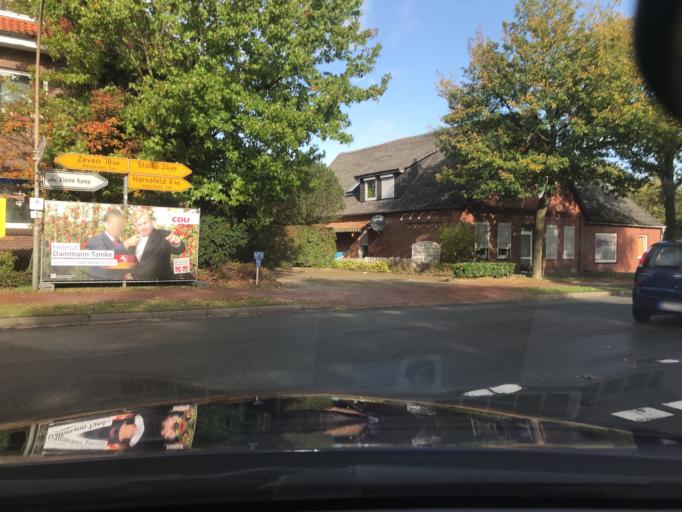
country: DE
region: Lower Saxony
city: Ahlerstedt
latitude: 53.4032
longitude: 9.4505
